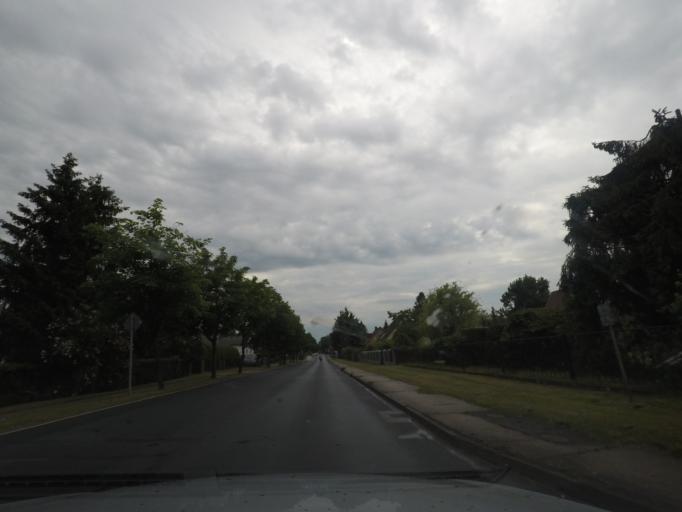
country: DE
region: Brandenburg
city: Hoppegarten
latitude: 52.5347
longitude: 13.6411
